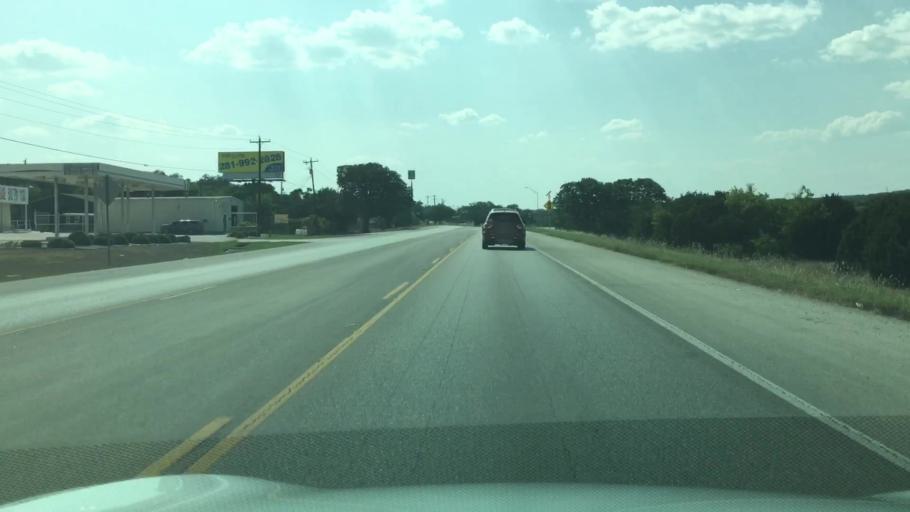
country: US
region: Texas
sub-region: Hays County
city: Wimberley
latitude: 29.9407
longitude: -98.0872
